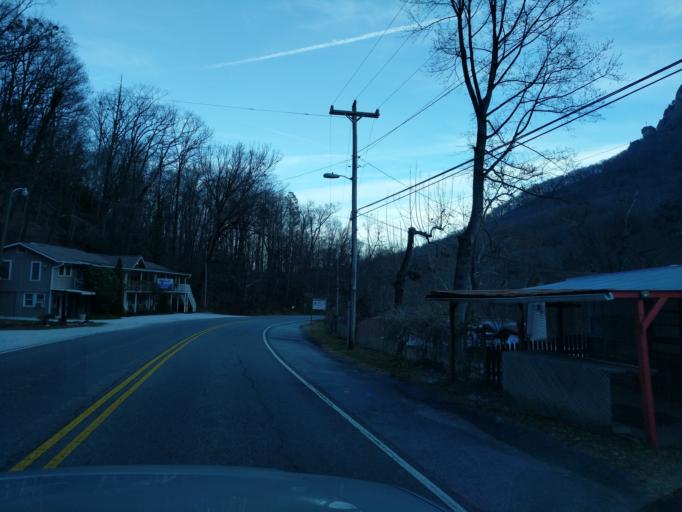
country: US
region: North Carolina
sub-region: Rutherford County
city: Lake Lure
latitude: 35.4417
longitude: -82.2569
